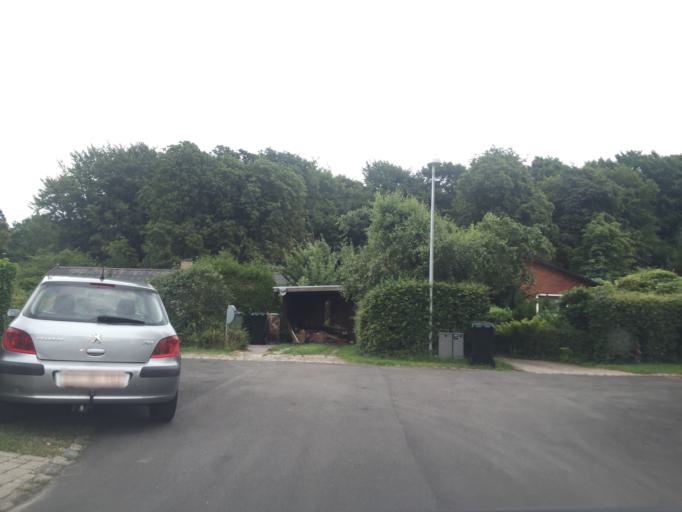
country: DK
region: Capital Region
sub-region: Rudersdal Kommune
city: Trorod
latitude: 55.7947
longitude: 12.5436
